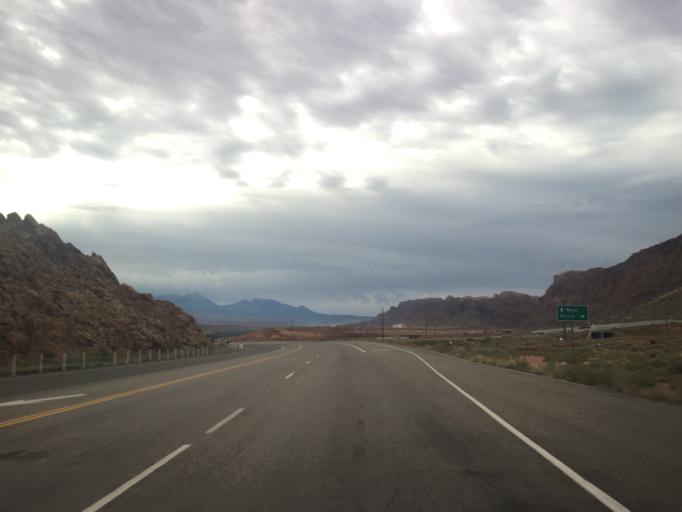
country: US
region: Utah
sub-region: Grand County
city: Moab
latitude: 38.6072
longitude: -109.6037
